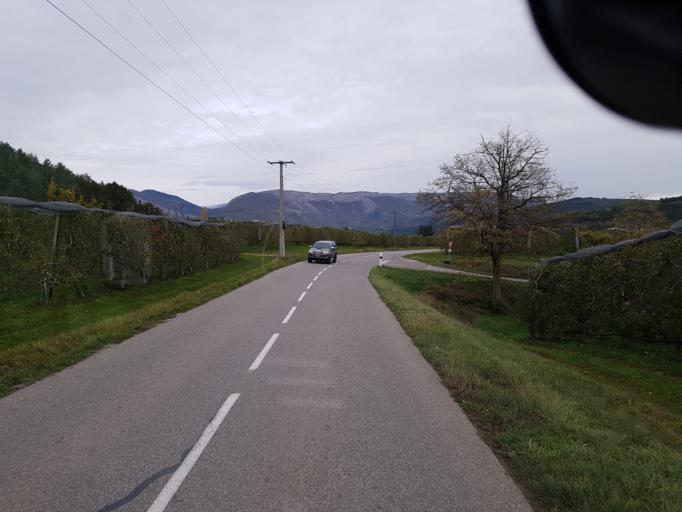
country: FR
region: Provence-Alpes-Cote d'Azur
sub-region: Departement des Hautes-Alpes
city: Laragne-Monteglin
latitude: 44.3301
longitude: 5.7483
